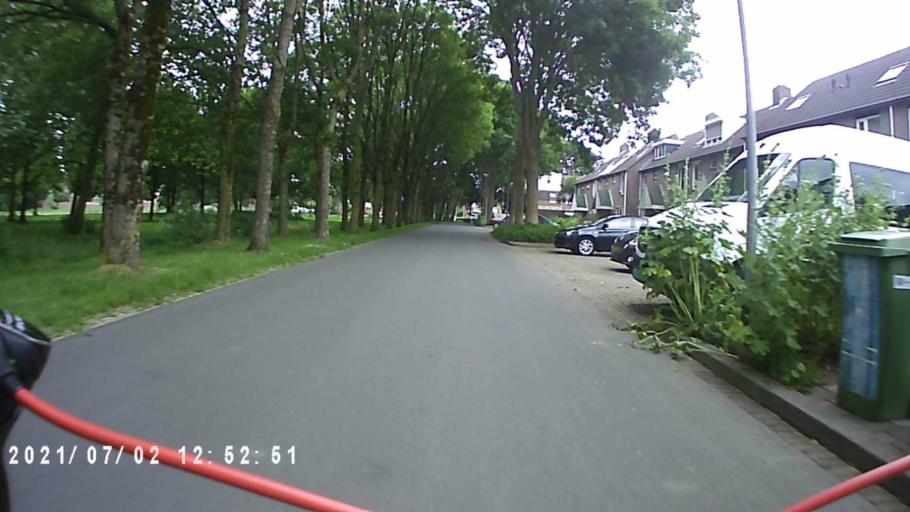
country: NL
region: Groningen
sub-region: Gemeente Groningen
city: Oosterpark
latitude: 53.2319
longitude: 6.5965
